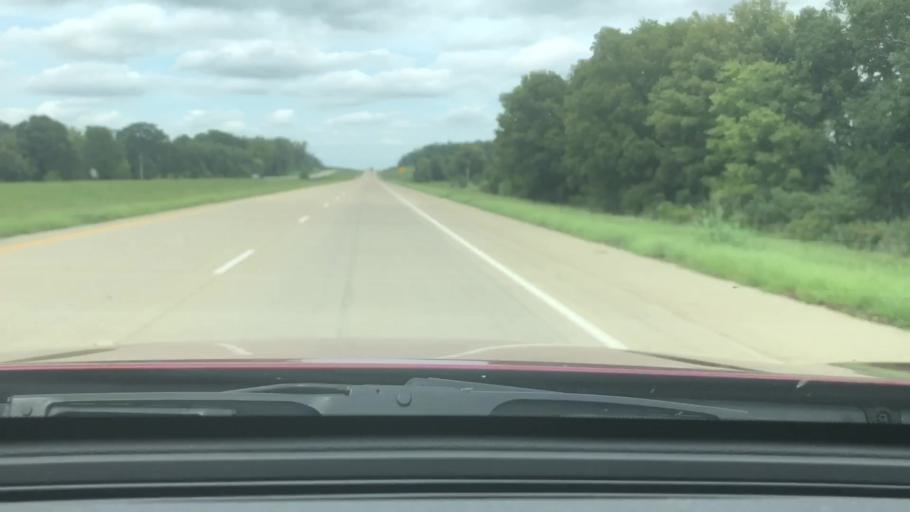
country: US
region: Louisiana
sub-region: Caddo Parish
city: Oil City
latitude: 32.7843
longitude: -93.8882
